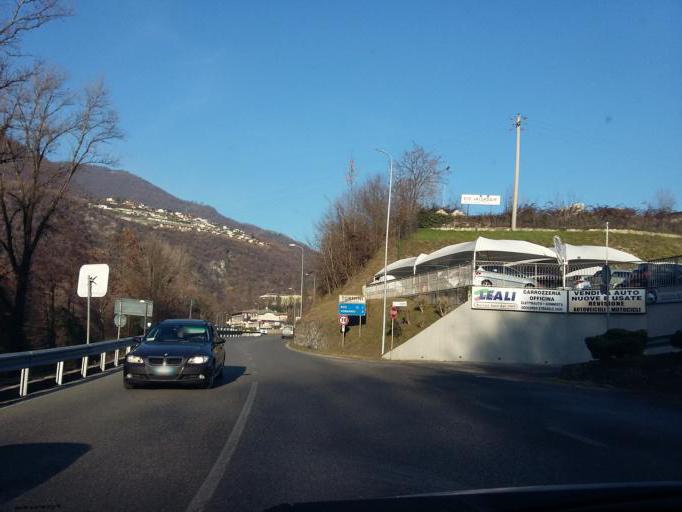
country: IT
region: Lombardy
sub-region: Provincia di Brescia
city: Roe Volciano
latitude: 45.6141
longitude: 10.4826
